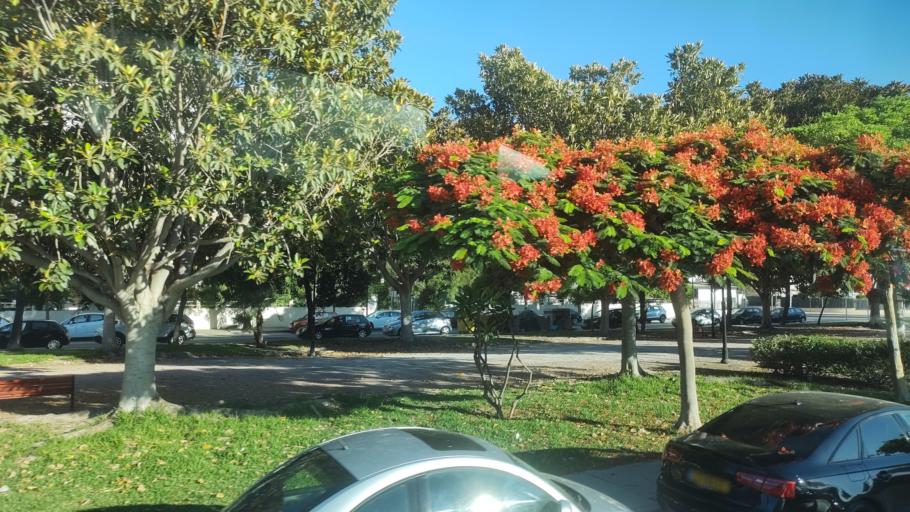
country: ES
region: Andalusia
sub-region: Provincia de Malaga
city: Torremolinos
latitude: 36.6380
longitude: -4.4889
